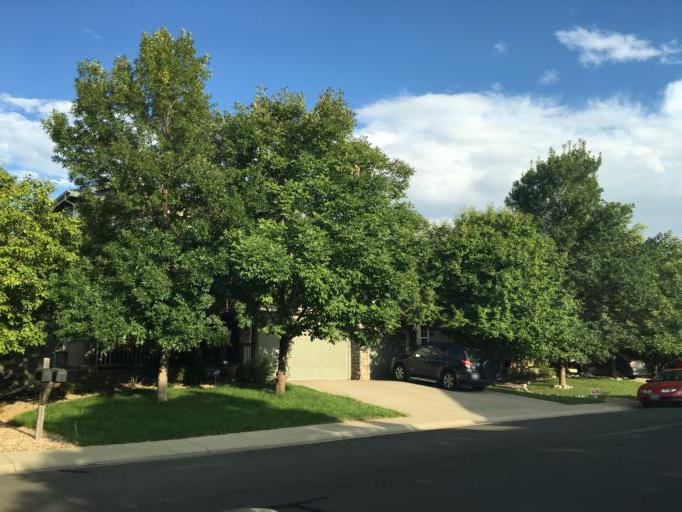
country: US
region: Colorado
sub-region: Adams County
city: Northglenn
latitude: 39.9490
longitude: -104.9530
